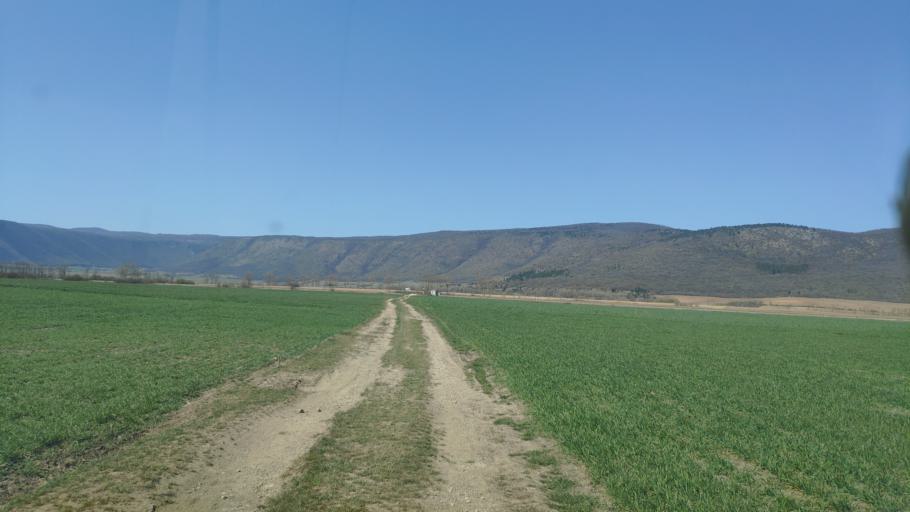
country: SK
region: Kosicky
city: Moldava nad Bodvou
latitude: 48.6023
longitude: 20.9293
